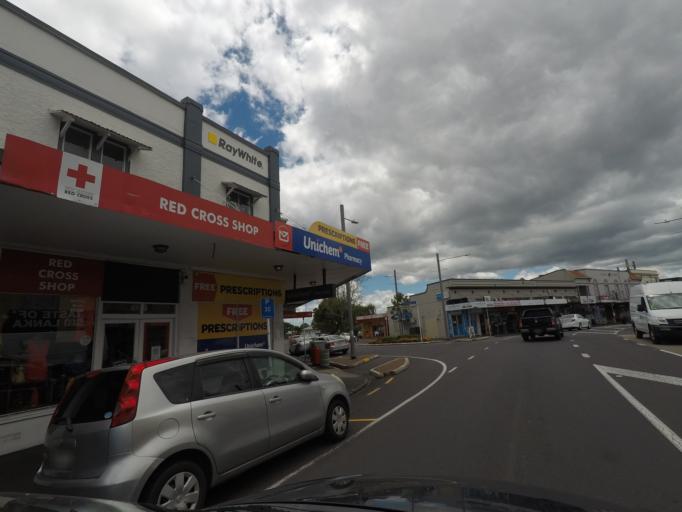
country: NZ
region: Auckland
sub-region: Auckland
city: Auckland
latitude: -36.8923
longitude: 174.7363
